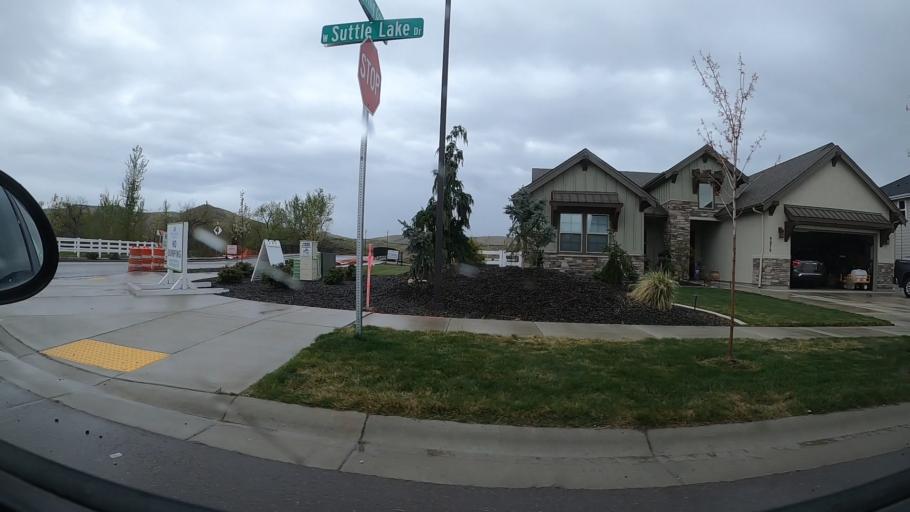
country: US
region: Idaho
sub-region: Ada County
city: Eagle
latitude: 43.7324
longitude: -116.2953
